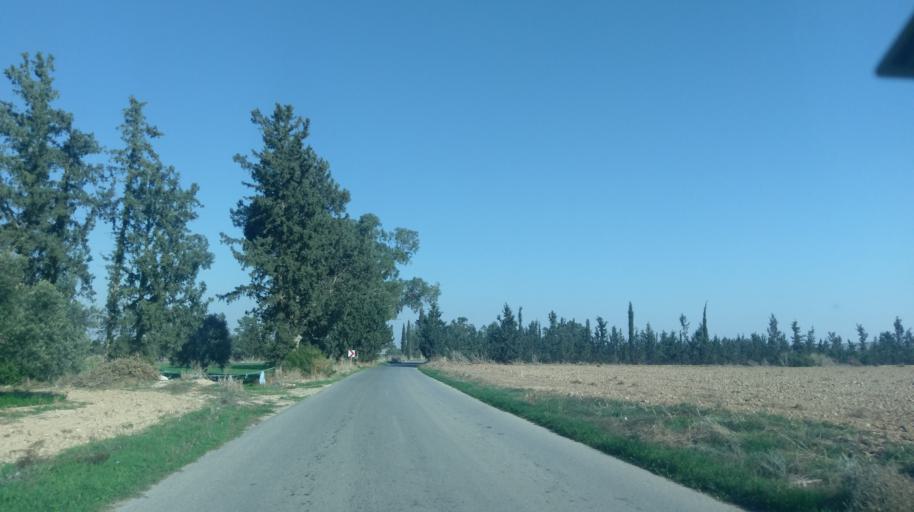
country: CY
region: Larnaka
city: Troulloi
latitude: 35.0828
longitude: 33.5965
